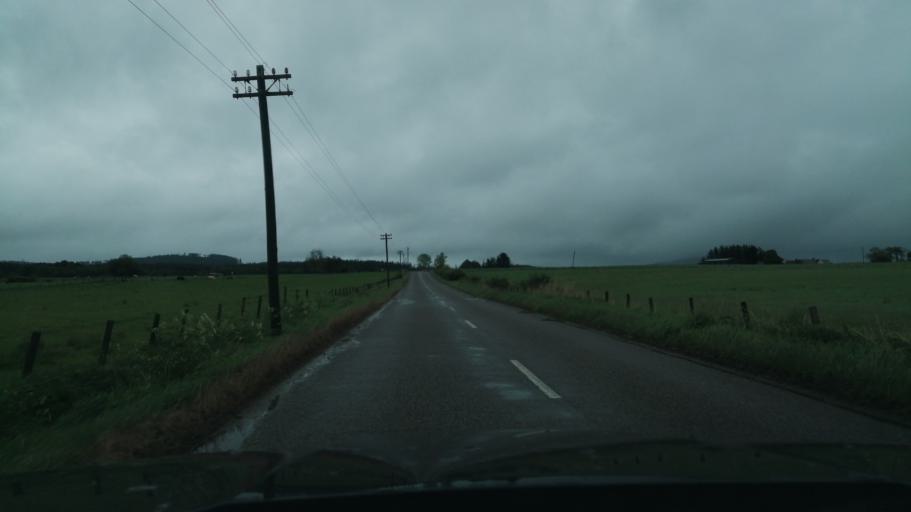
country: GB
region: Scotland
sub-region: Aberdeenshire
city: Huntly
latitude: 57.5392
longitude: -2.7803
